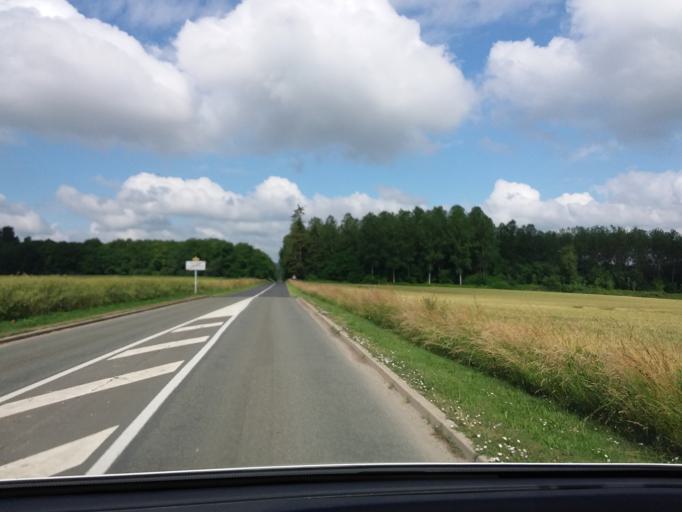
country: FR
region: Champagne-Ardenne
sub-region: Departement de la Marne
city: Fismes
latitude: 49.3774
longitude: 3.6717
